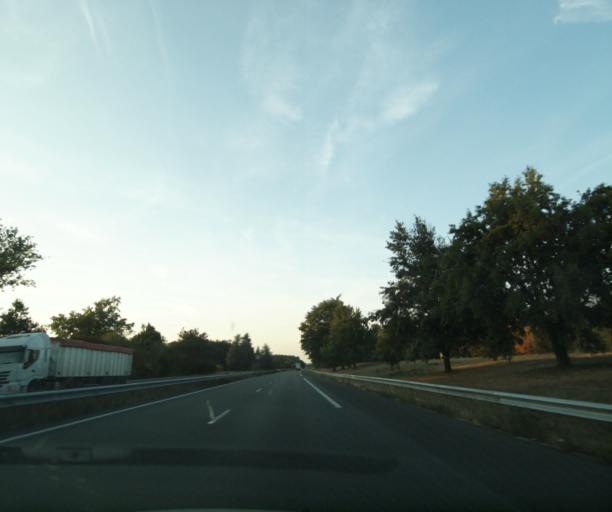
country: FR
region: Aquitaine
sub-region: Departement du Lot-et-Garonne
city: Damazan
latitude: 44.3430
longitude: 0.2513
